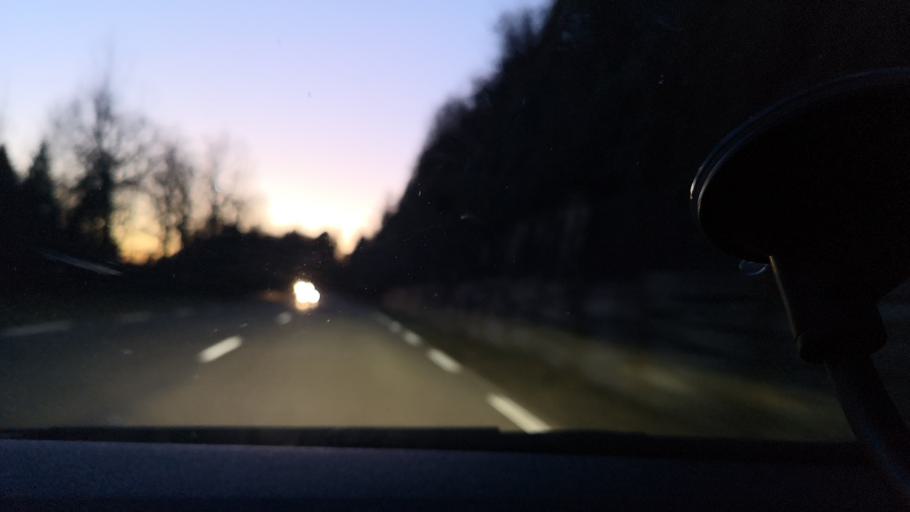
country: FR
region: Franche-Comte
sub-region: Departement du Jura
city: Champagnole
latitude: 46.7559
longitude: 5.9591
